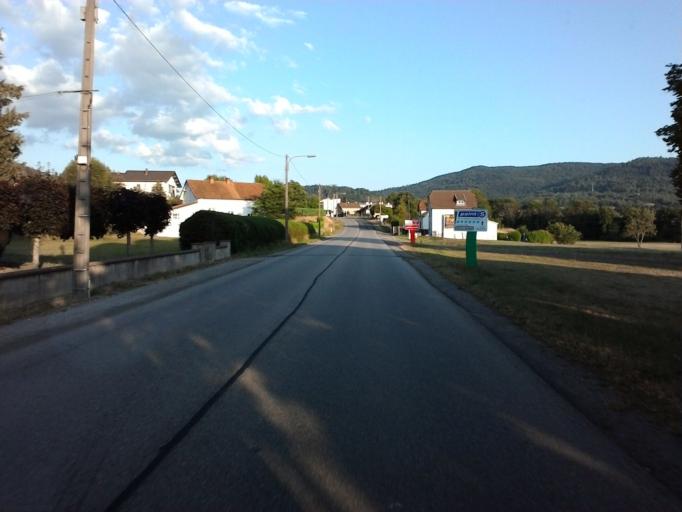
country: FR
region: Lorraine
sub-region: Departement des Vosges
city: Le Thillot
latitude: 47.8861
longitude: 6.7540
